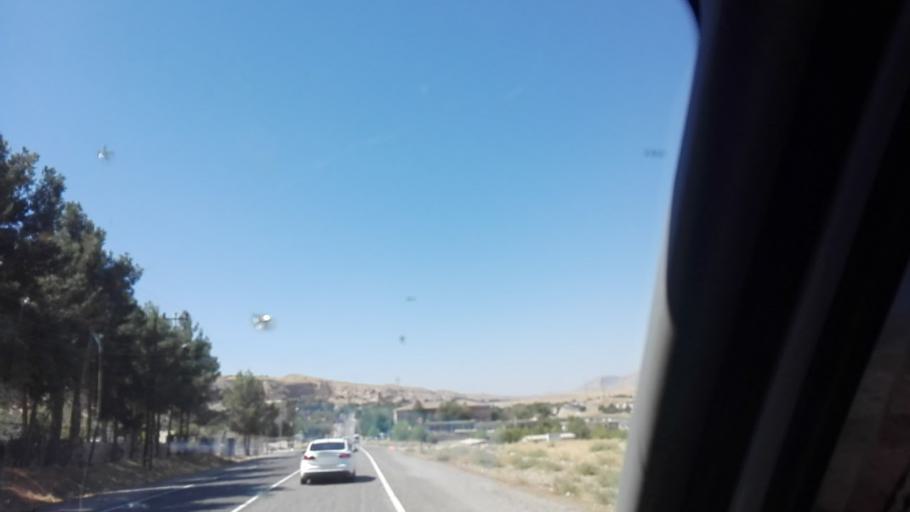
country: TR
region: Batman
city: Hasankeyf
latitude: 37.7137
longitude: 41.4280
